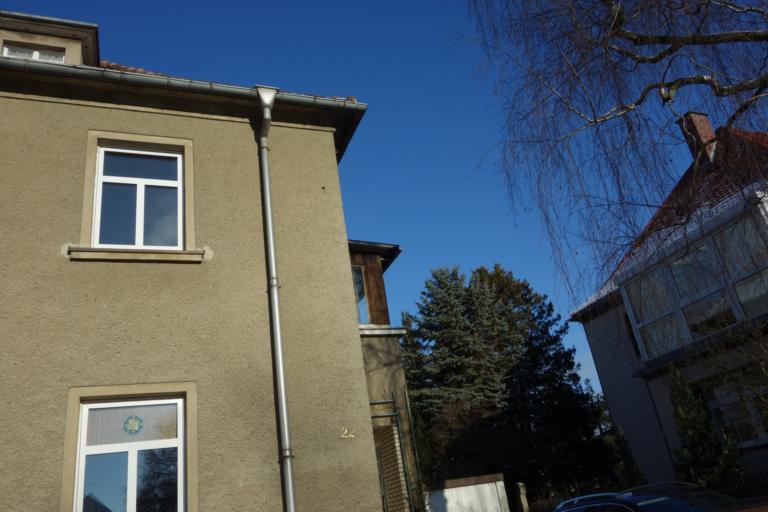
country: DE
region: Saxony
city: Freiberg
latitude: 50.9190
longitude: 13.3336
